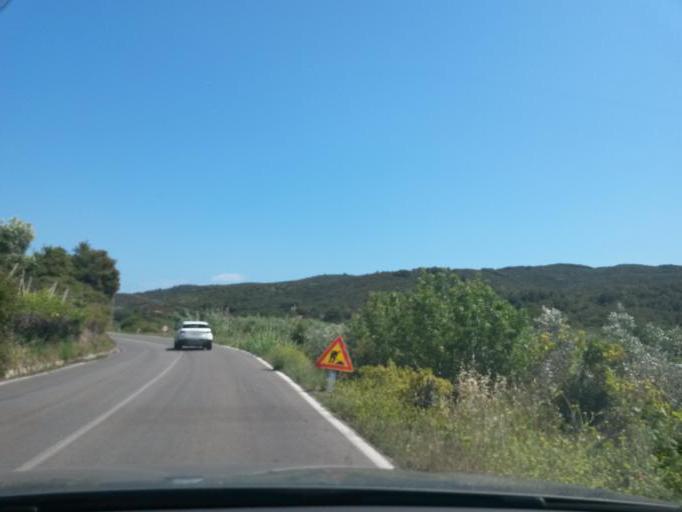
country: IT
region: Tuscany
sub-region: Provincia di Livorno
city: Campo nell'Elba
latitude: 42.7425
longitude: 10.2117
